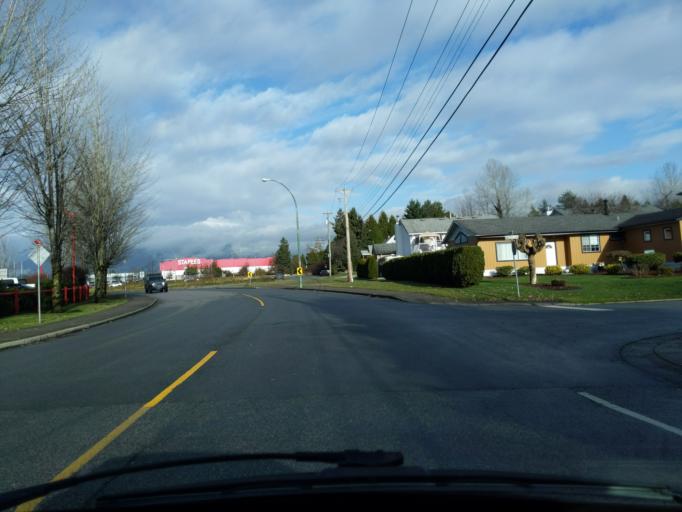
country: CA
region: British Columbia
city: Pitt Meadows
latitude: 49.2186
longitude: -122.6648
